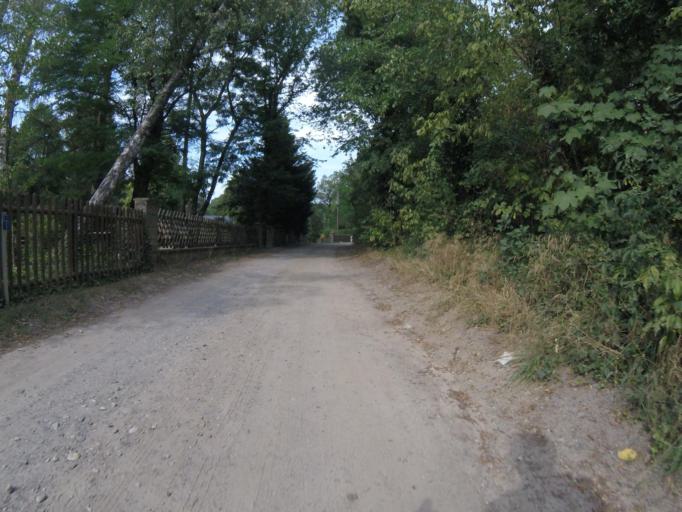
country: DE
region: Brandenburg
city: Wildau
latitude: 52.3199
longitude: 13.7192
